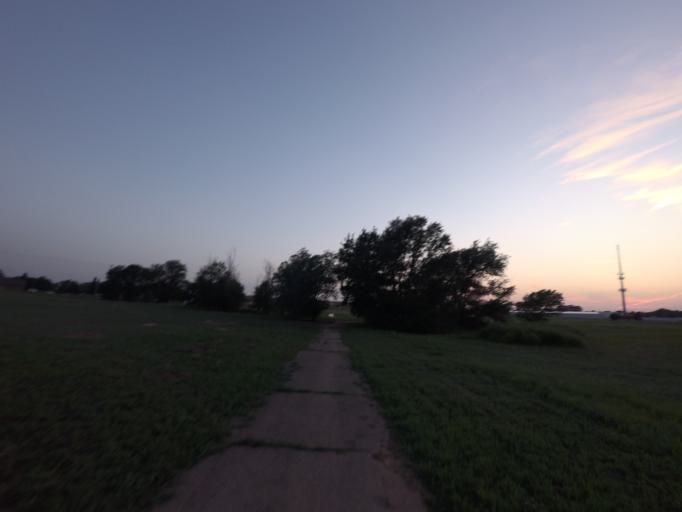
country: US
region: New Mexico
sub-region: Curry County
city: Clovis
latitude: 34.4276
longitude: -103.1891
